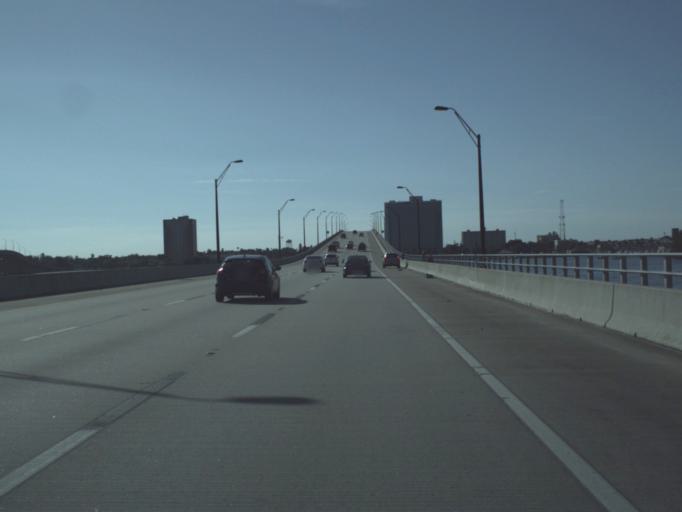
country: US
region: Florida
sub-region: Lee County
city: North Fort Myers
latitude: 26.6570
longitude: -81.8733
